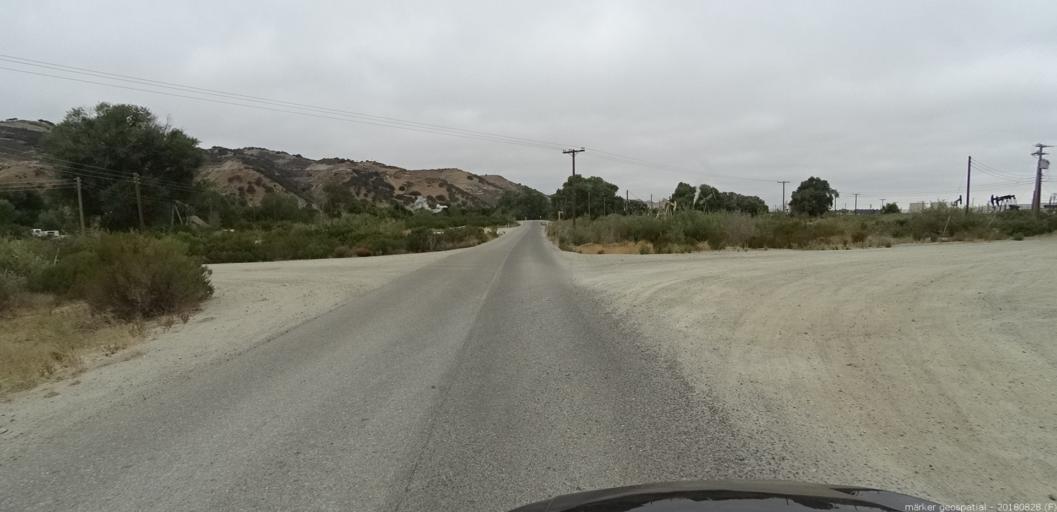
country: US
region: California
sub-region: San Luis Obispo County
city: Lake Nacimiento
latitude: 35.9549
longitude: -120.8734
